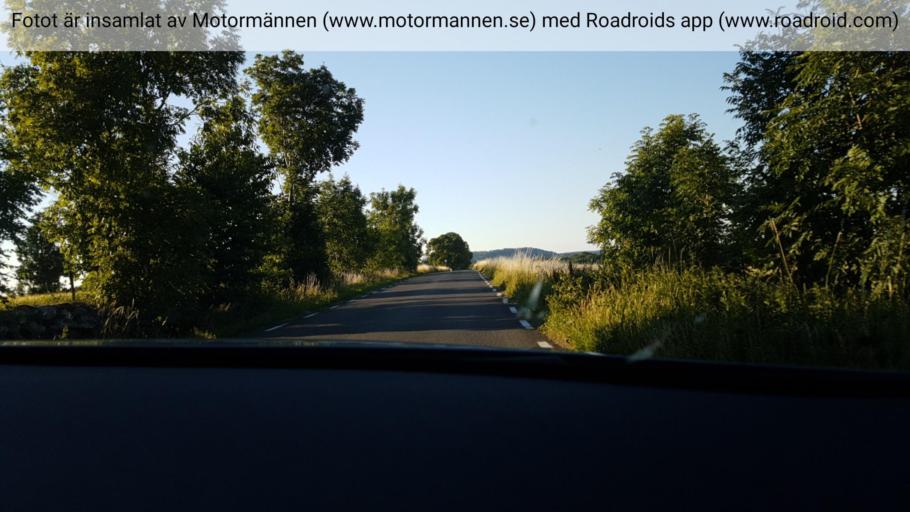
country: SE
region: Vaestra Goetaland
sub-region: Skovde Kommun
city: Skultorp
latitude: 58.2615
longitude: 13.7898
